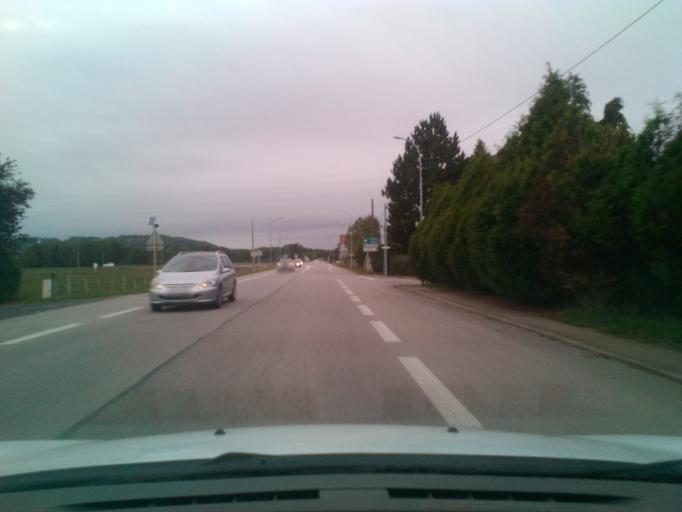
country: FR
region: Lorraine
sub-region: Departement des Vosges
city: Vincey
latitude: 48.3494
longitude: 6.3205
